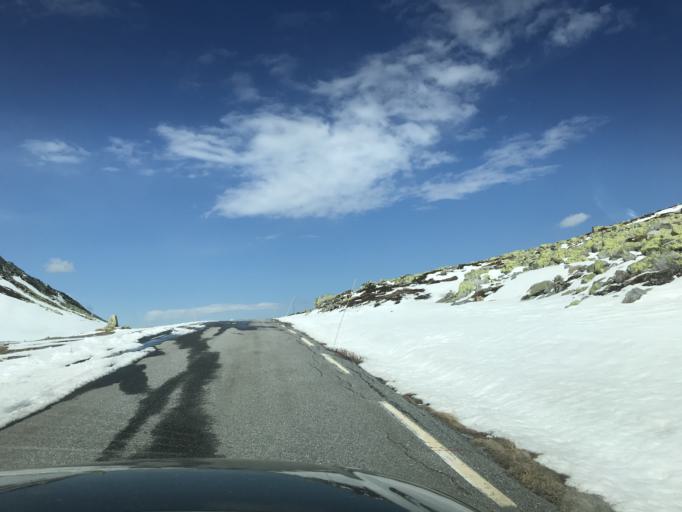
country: NO
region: Telemark
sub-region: Tinn
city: Rjukan
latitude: 59.8177
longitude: 8.7226
